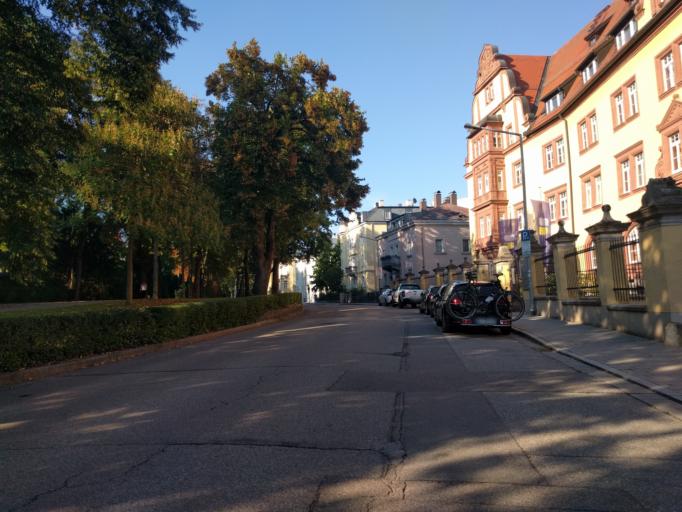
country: DE
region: Bavaria
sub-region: Upper Palatinate
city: Regensburg
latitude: 49.0159
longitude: 12.1073
